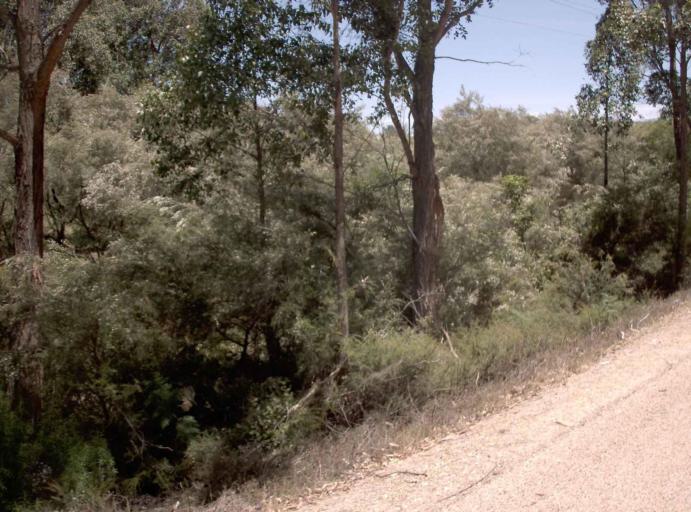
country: AU
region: Victoria
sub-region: East Gippsland
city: Bairnsdale
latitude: -37.7330
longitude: 147.7823
